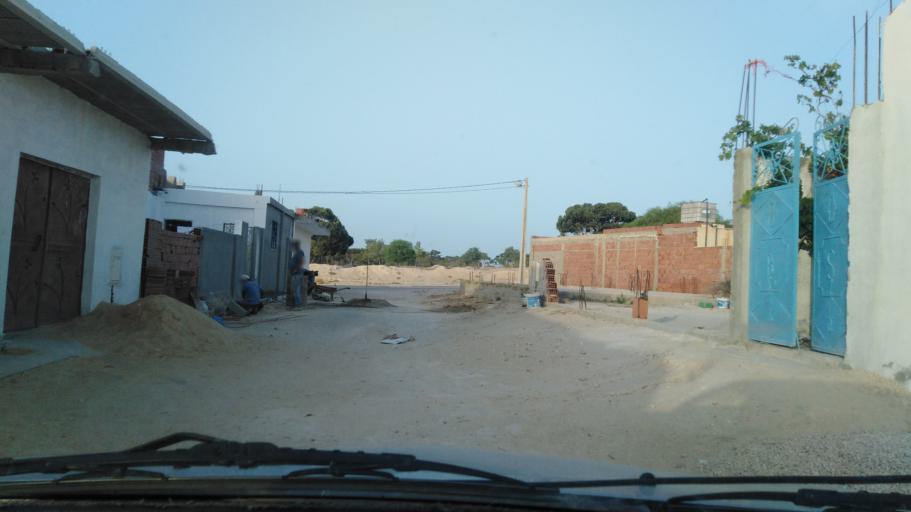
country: TN
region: Qabis
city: Gabes
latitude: 33.9517
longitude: 9.9965
